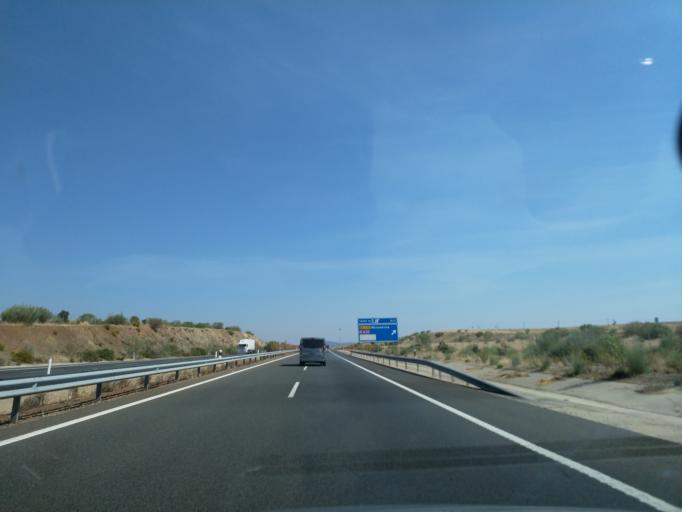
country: ES
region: Extremadura
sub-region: Provincia de Badajoz
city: Merida
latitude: 38.9638
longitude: -6.3403
